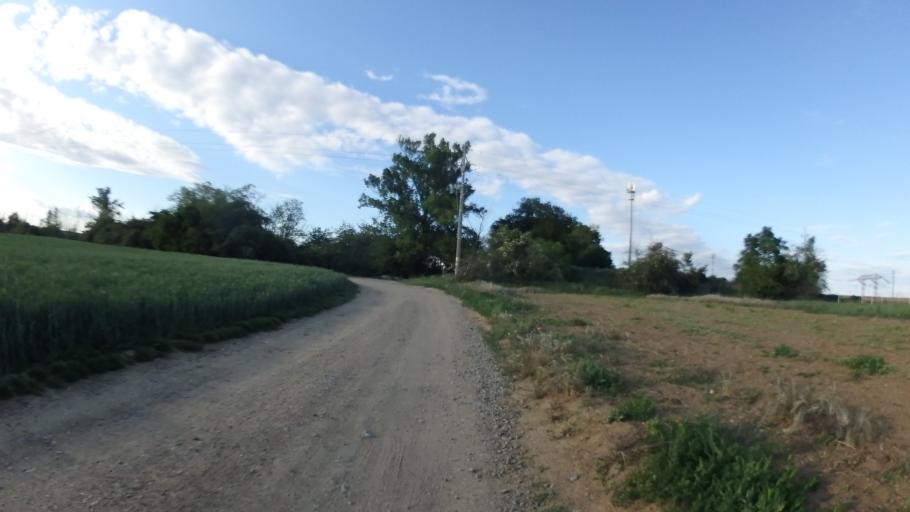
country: CZ
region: South Moravian
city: Ostopovice
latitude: 49.1450
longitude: 16.5547
